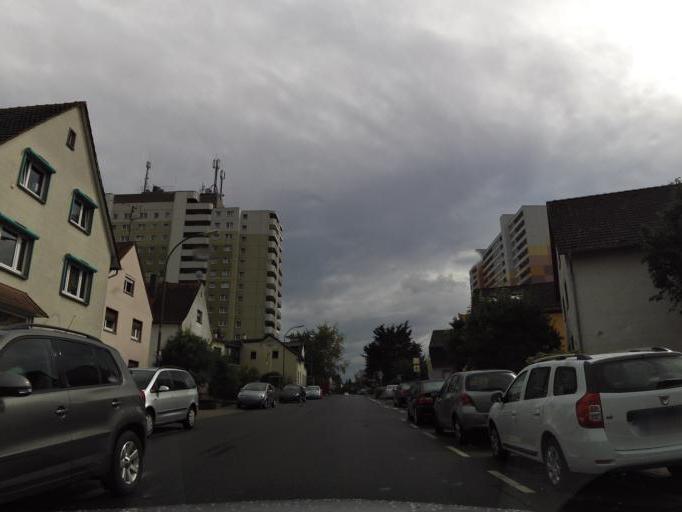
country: DE
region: Hesse
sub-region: Regierungsbezirk Darmstadt
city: Bad Homburg vor der Hoehe
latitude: 50.1912
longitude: 8.6666
